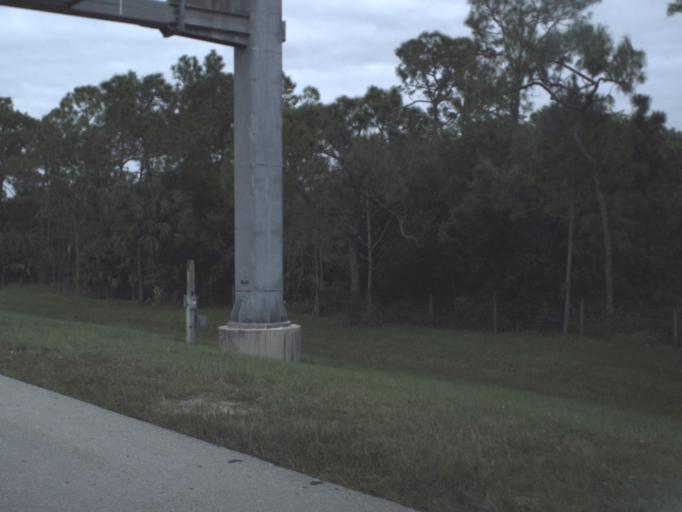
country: US
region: Florida
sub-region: Lee County
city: Bonita Springs
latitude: 26.3055
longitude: -81.7428
